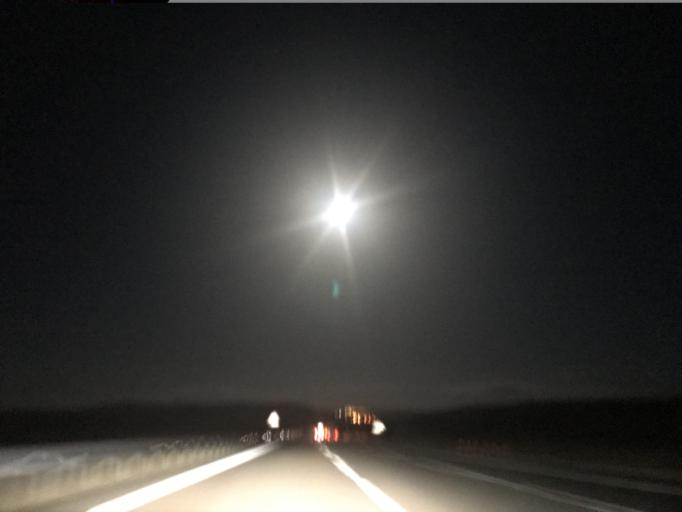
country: TR
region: Nigde
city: Ulukisla
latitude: 37.6353
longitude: 34.4278
